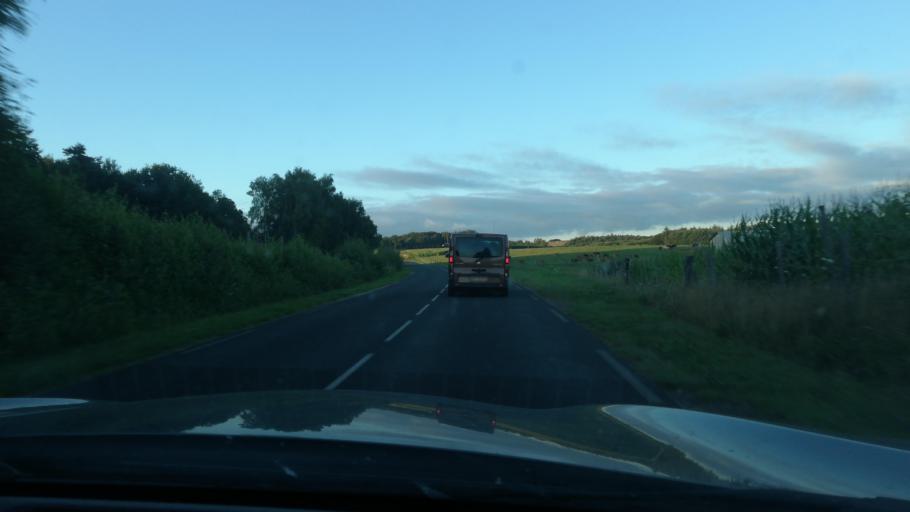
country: FR
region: Auvergne
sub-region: Departement du Cantal
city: Laroquebrou
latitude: 44.9447
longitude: 2.0897
